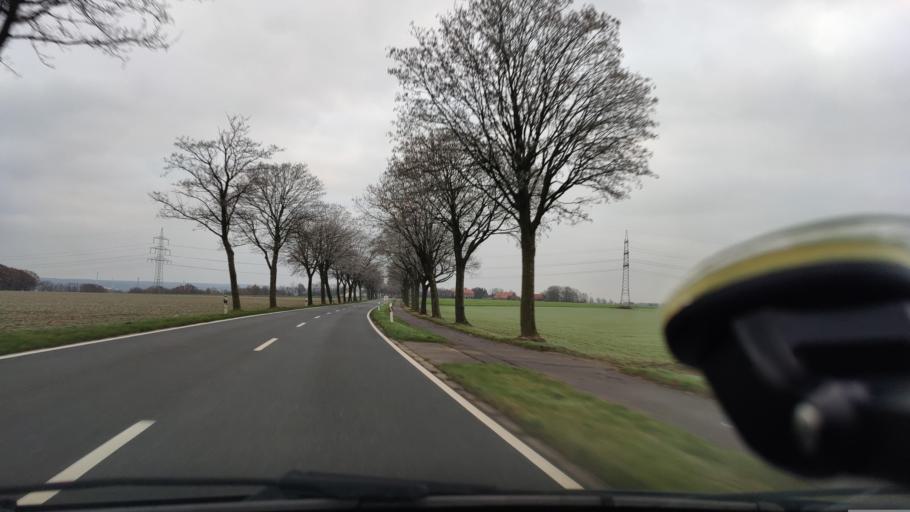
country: DE
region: North Rhine-Westphalia
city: Kalkar
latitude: 51.7178
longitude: 6.3031
